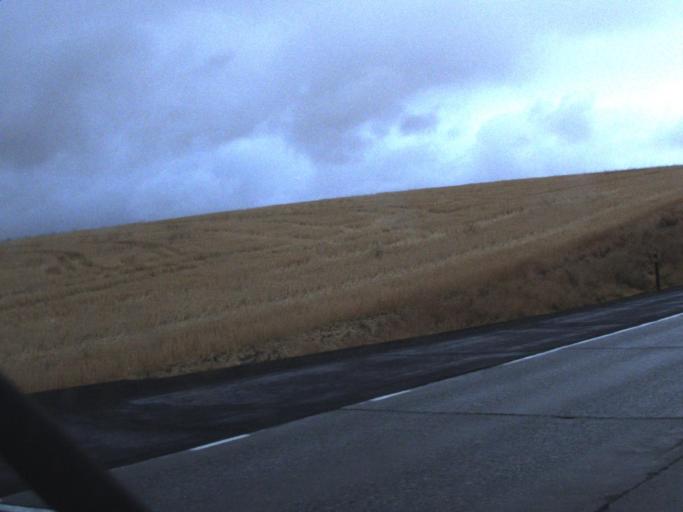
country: US
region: Washington
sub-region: Whitman County
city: Colfax
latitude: 47.1151
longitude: -117.3791
